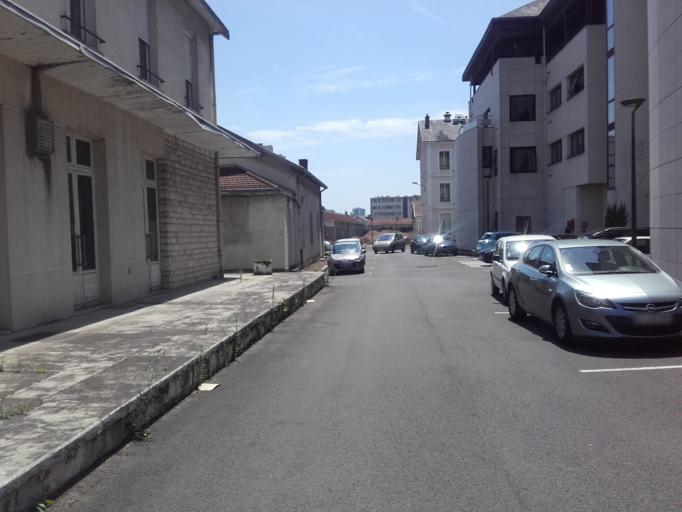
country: FR
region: Centre
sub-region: Departement d'Indre-et-Loire
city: La Riche
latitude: 47.3838
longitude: 0.6754
